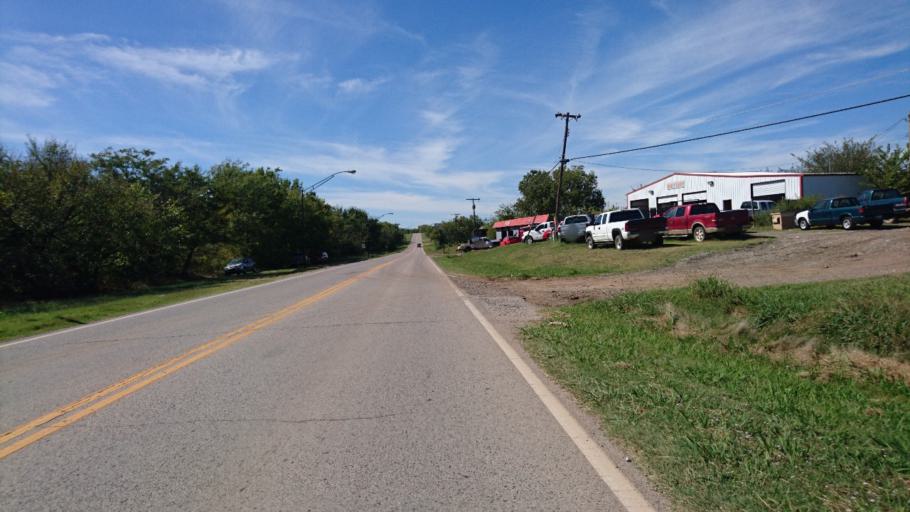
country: US
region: Oklahoma
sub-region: Lincoln County
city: Stroud
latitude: 35.7495
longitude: -96.6655
